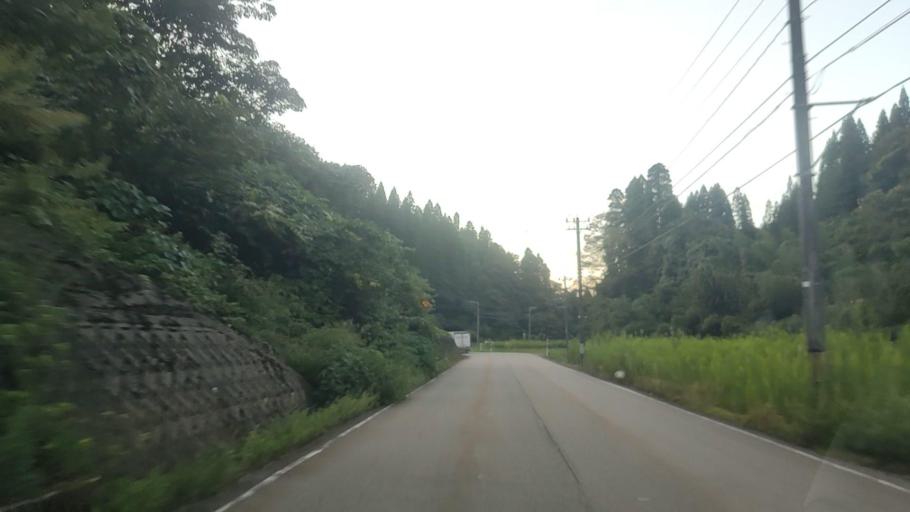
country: JP
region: Ishikawa
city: Tsubata
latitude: 36.6363
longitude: 136.7694
